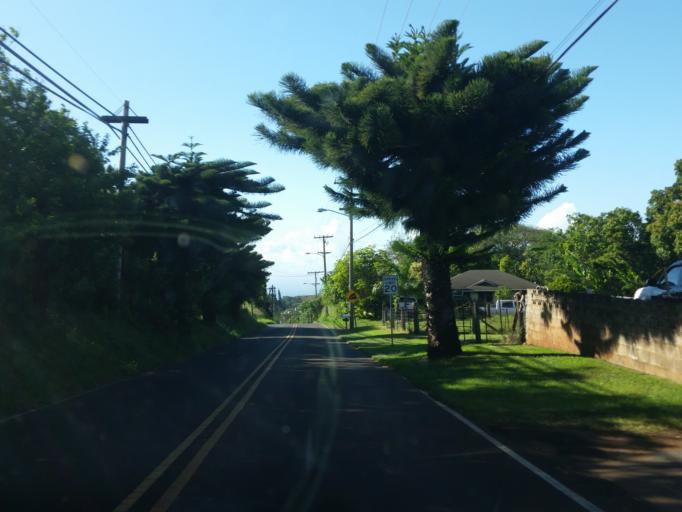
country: US
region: Hawaii
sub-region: Maui County
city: Makawao
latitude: 20.8503
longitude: -156.3087
